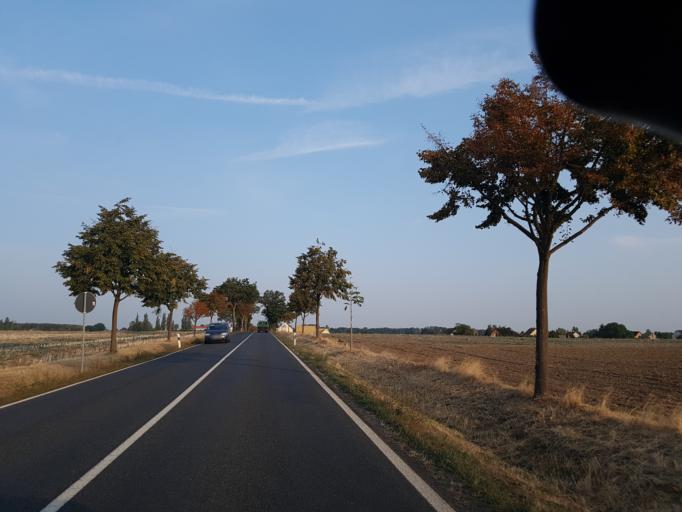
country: DE
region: Saxony
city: Elsnig
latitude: 51.6094
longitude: 12.9244
